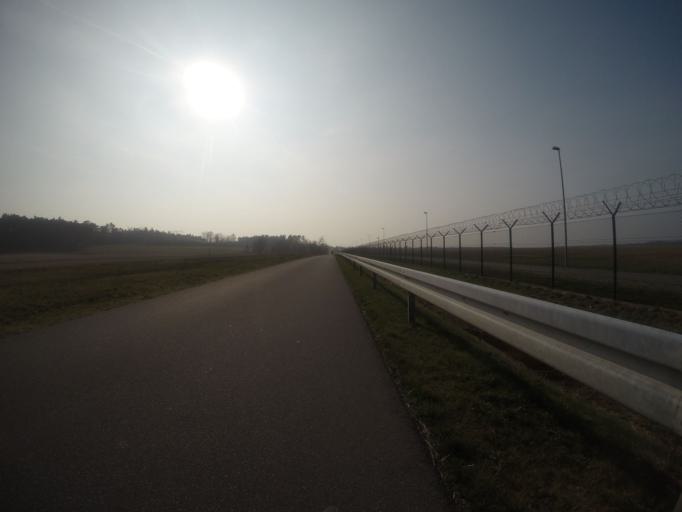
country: DE
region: Brandenburg
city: Schonefeld
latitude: 52.3427
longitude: 13.4700
